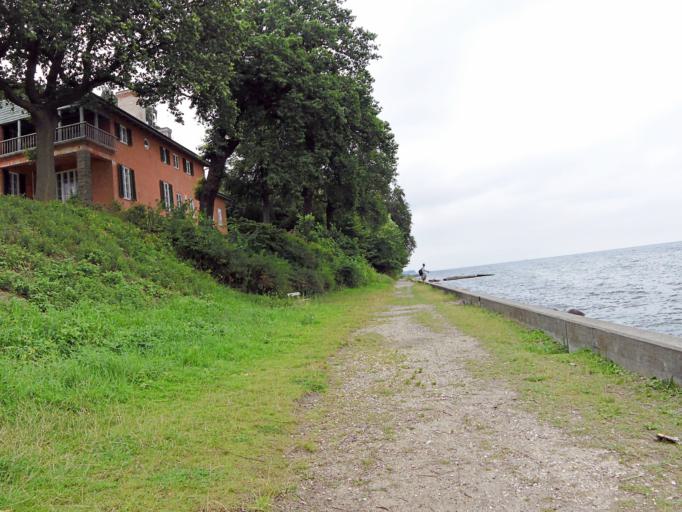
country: DK
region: Capital Region
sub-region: Gentofte Kommune
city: Charlottenlund
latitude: 55.7995
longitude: 12.5889
